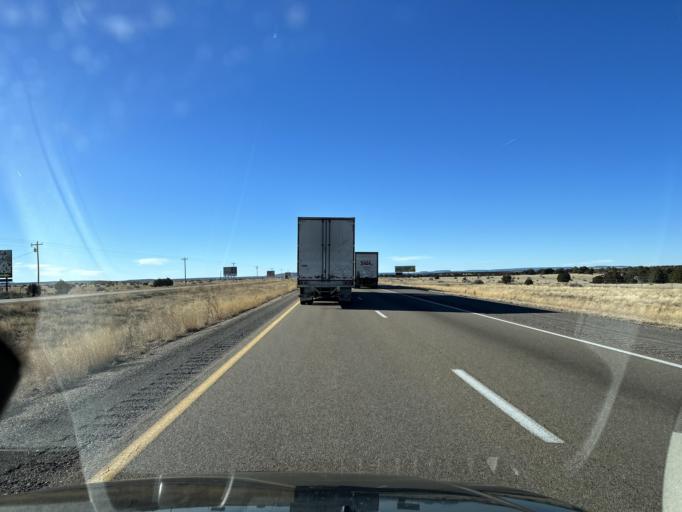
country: US
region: New Mexico
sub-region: San Miguel County
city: Las Vegas
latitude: 34.9938
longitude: -105.3373
